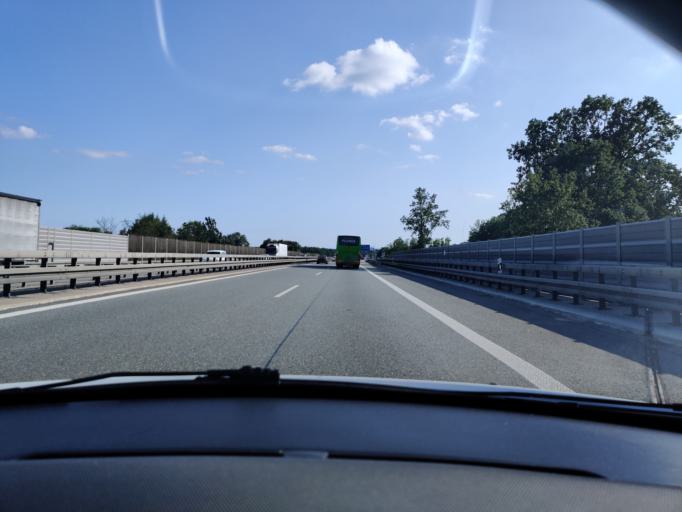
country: DE
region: Bavaria
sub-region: Upper Palatinate
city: Wackersdorf
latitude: 49.3204
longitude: 12.1545
